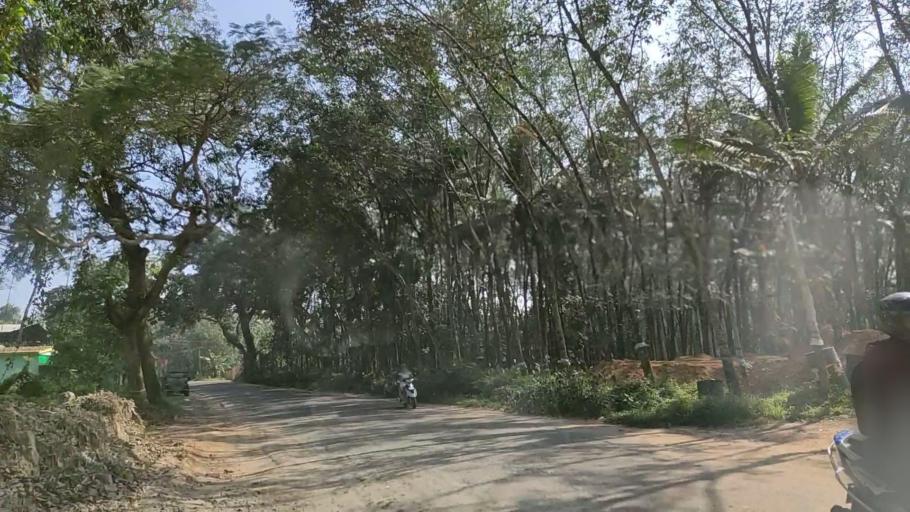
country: IN
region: Kerala
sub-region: Kollam
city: Punalur
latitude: 8.9046
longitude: 76.8734
